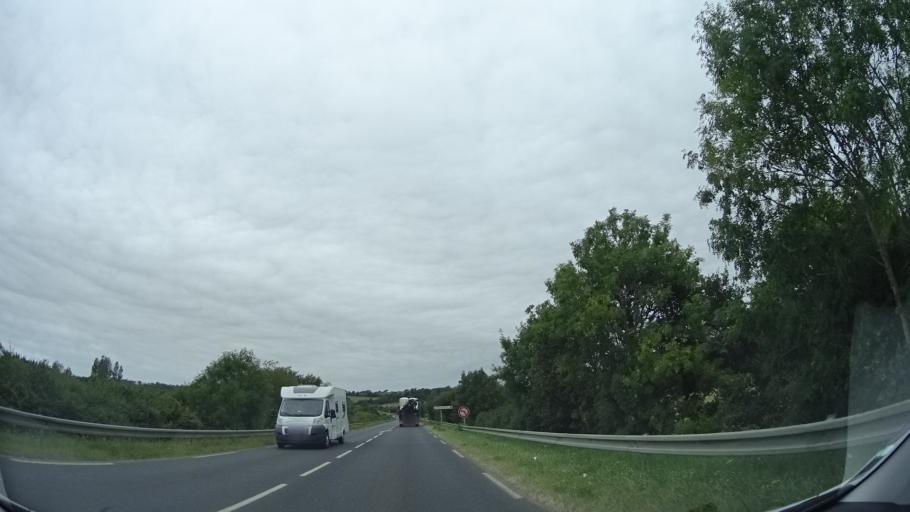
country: FR
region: Lower Normandy
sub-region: Departement de la Manche
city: Barneville-Plage
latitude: 49.3840
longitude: -1.7479
